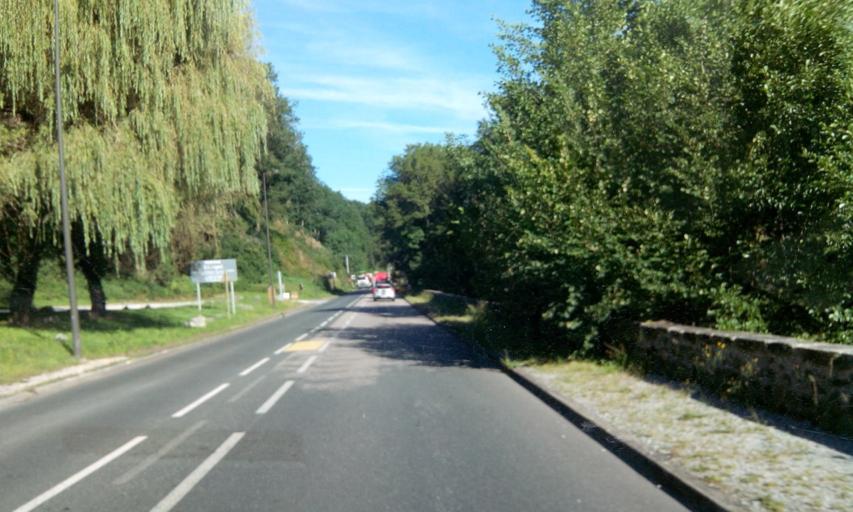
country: FR
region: Limousin
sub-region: Departement de la Haute-Vienne
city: Saint-Leonard-de-Noblat
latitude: 45.8347
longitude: 1.4731
